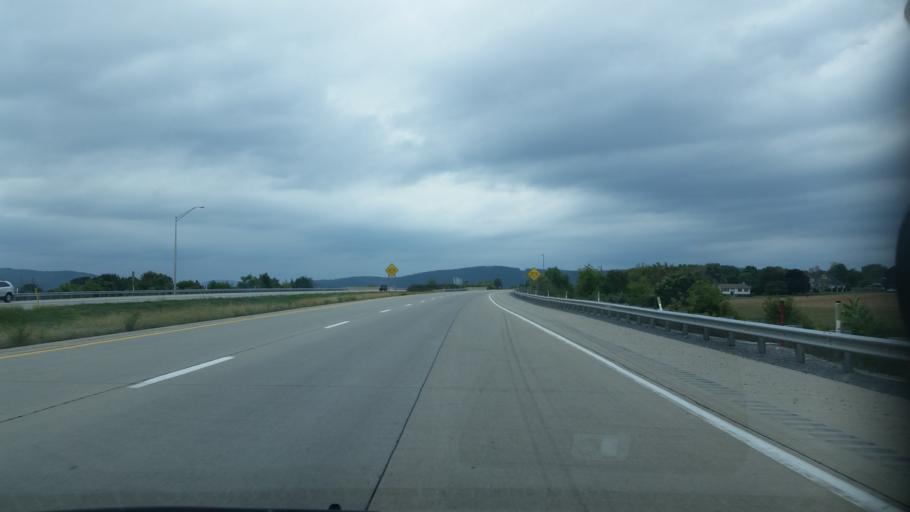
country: US
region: Pennsylvania
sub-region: Centre County
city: Pleasant Gap
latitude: 40.8941
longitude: -77.7349
